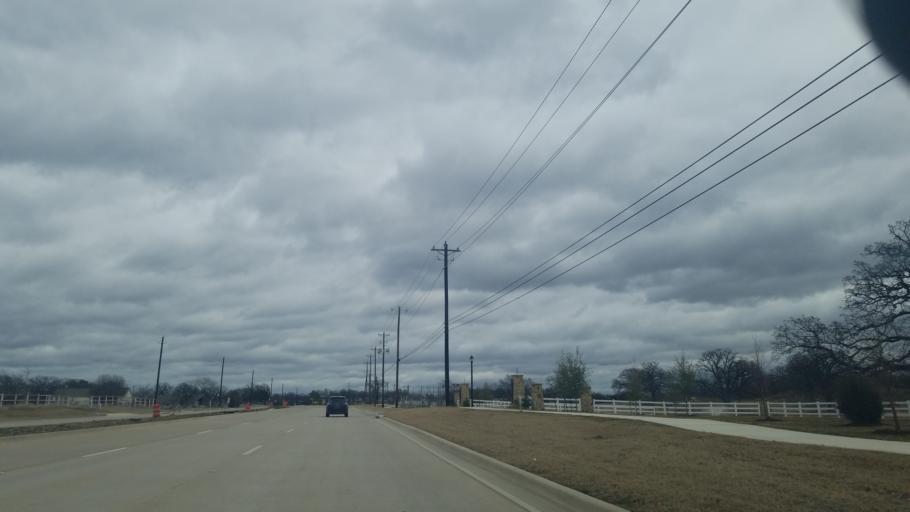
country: US
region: Texas
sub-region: Denton County
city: Bartonville
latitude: 33.0471
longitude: -97.1344
